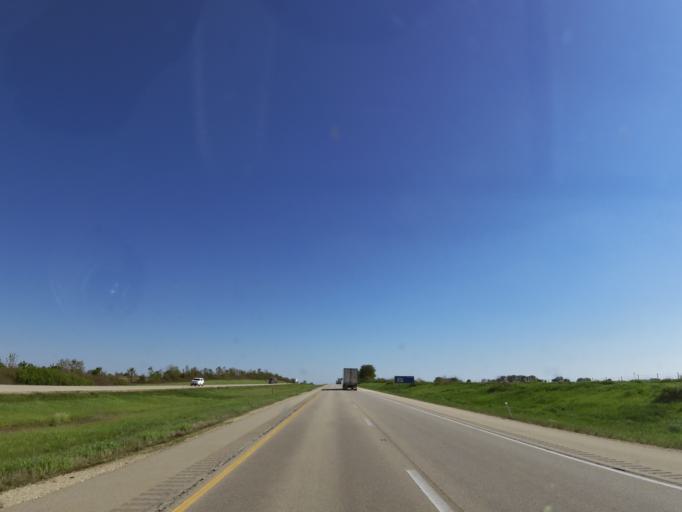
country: US
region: Illinois
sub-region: Ogle County
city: Rochelle
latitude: 41.7864
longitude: -89.0103
